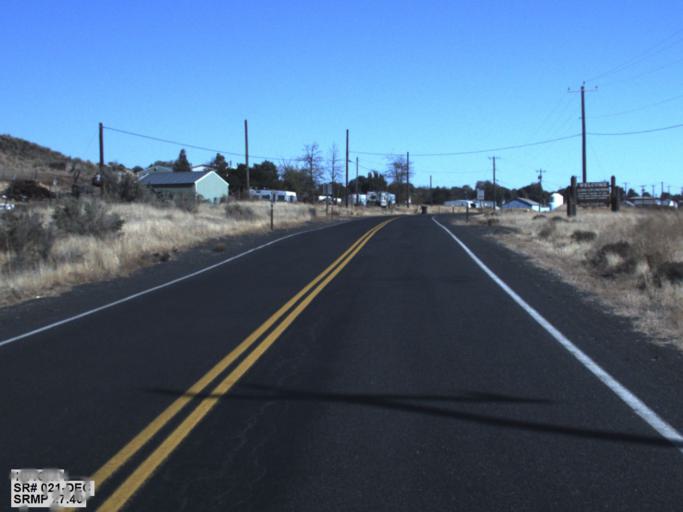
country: US
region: Washington
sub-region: Adams County
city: Ritzville
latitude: 46.9712
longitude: -118.6294
